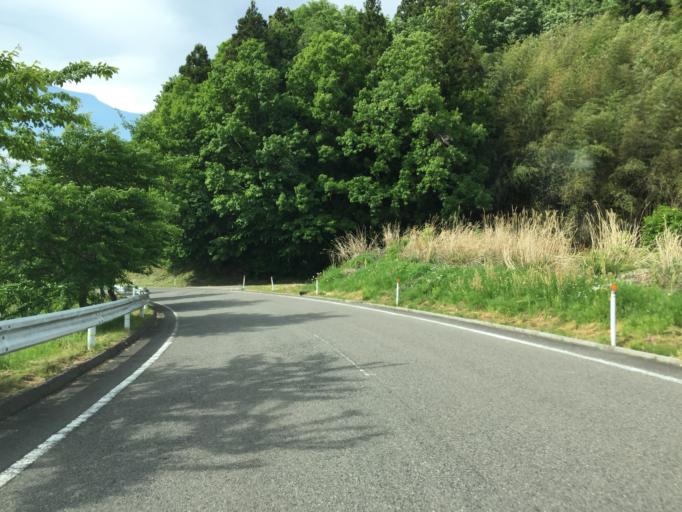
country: JP
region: Fukushima
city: Nihommatsu
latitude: 37.6104
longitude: 140.5260
